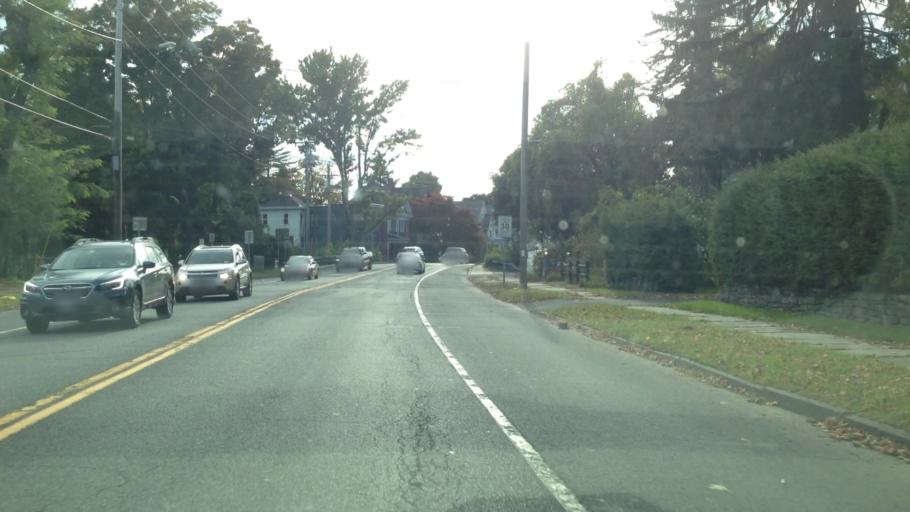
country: US
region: New York
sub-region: Ulster County
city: Kingston
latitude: 41.9334
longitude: -74.0084
